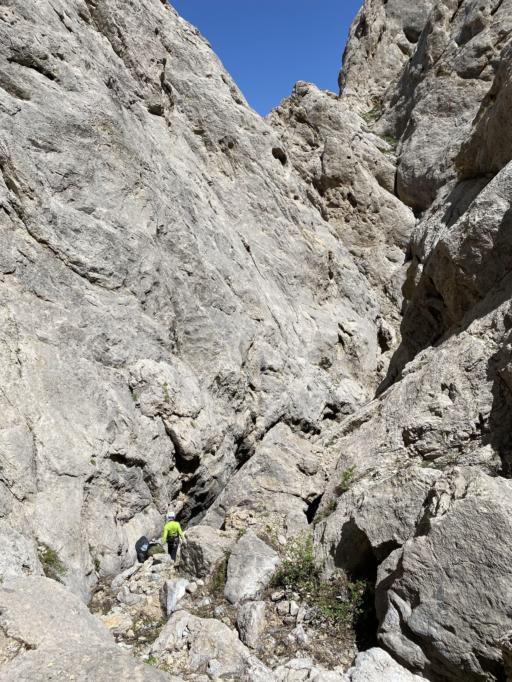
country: KZ
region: Ongtustik Qazaqstan
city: Ashchysay
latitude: 43.7681
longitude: 68.7941
